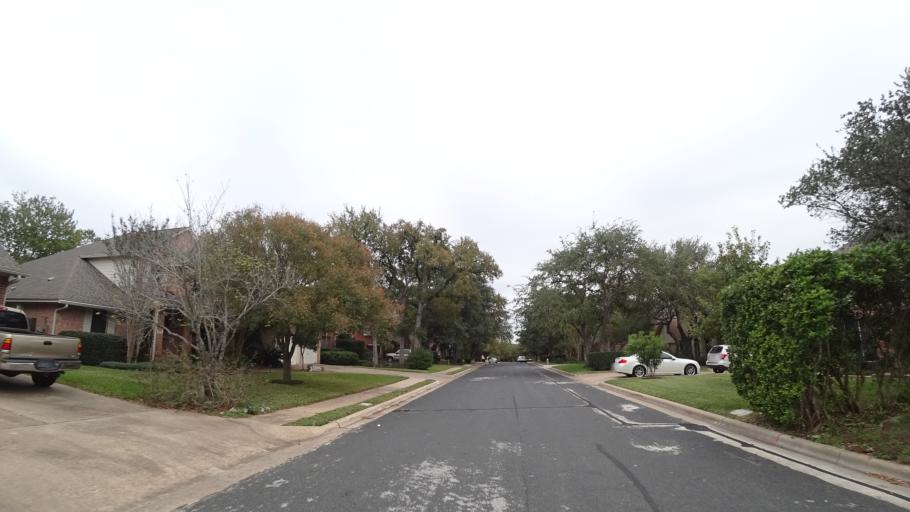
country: US
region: Texas
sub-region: Travis County
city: Shady Hollow
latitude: 30.1872
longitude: -97.8975
